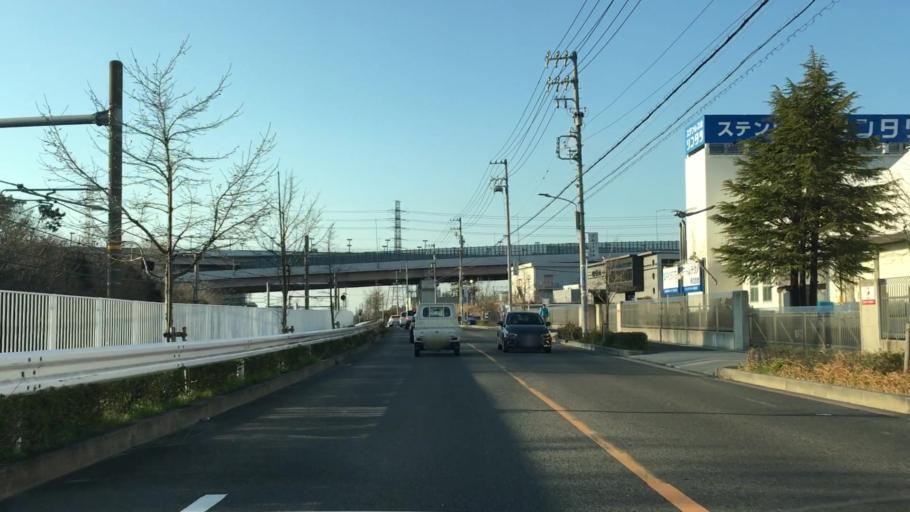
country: JP
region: Aichi
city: Obu
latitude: 35.0495
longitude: 136.9517
